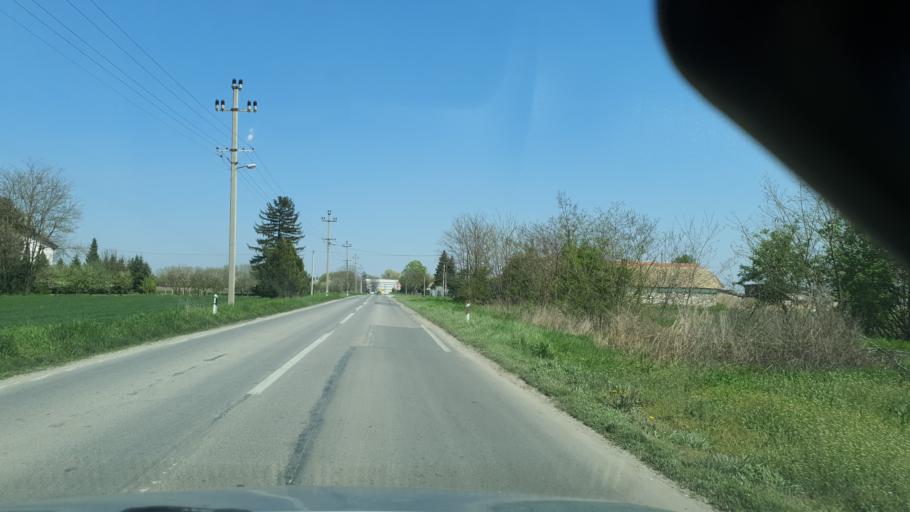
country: RS
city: Celarevo
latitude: 45.2728
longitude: 19.5460
